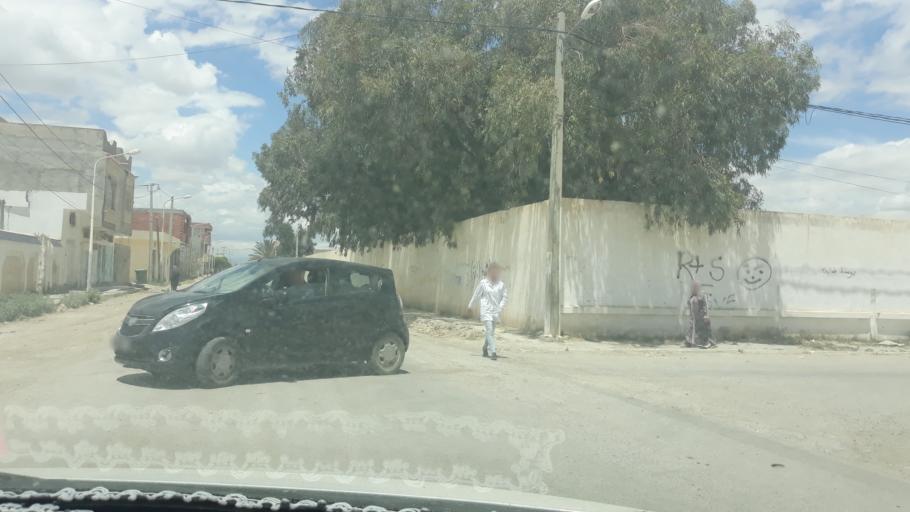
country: TN
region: Al Qayrawan
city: Kairouan
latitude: 35.6163
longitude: 9.9249
